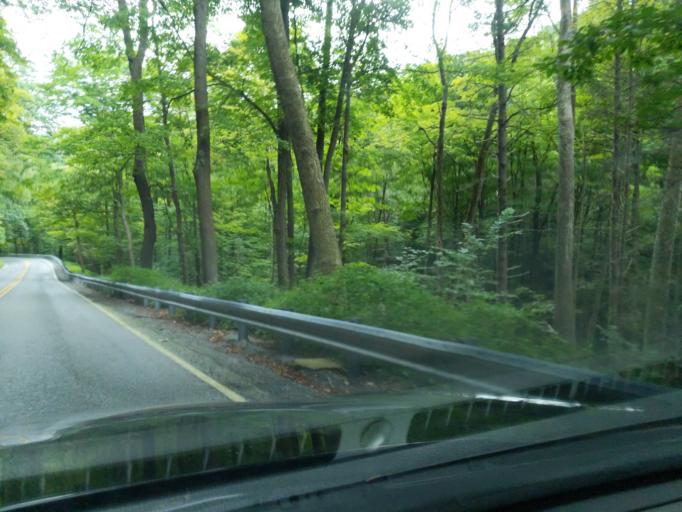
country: US
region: Pennsylvania
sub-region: Cambria County
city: Cresson
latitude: 40.3610
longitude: -78.5415
